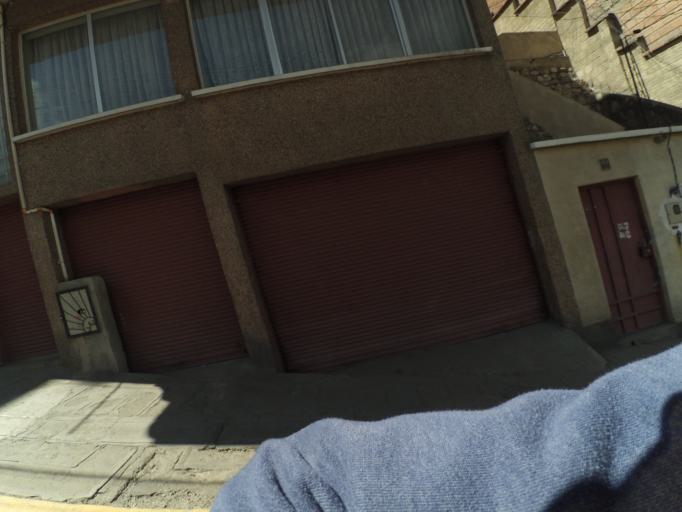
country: BO
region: La Paz
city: La Paz
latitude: -16.4945
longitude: -68.1296
